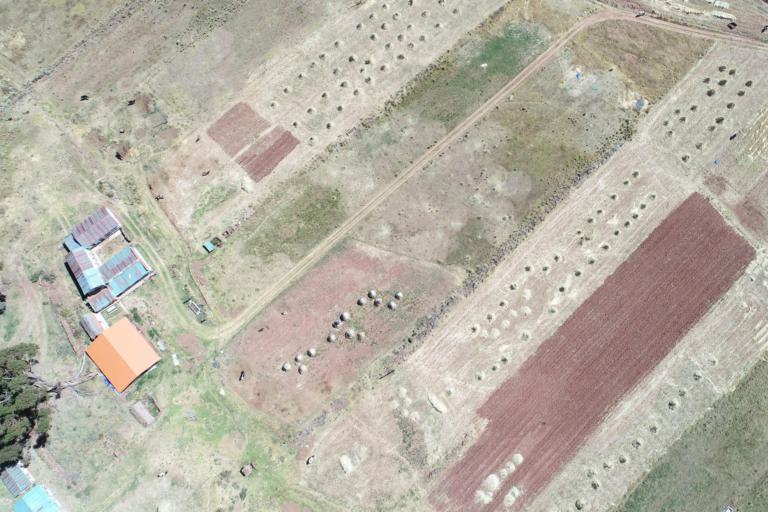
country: BO
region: La Paz
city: Tiahuanaco
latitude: -16.6028
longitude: -68.7756
